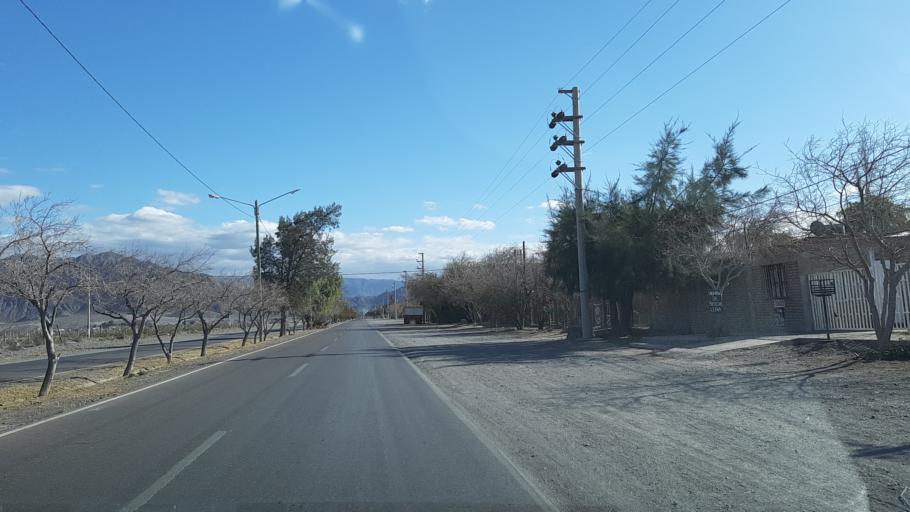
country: AR
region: San Juan
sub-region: Departamento de Rivadavia
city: Rivadavia
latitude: -31.5413
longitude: -68.6287
